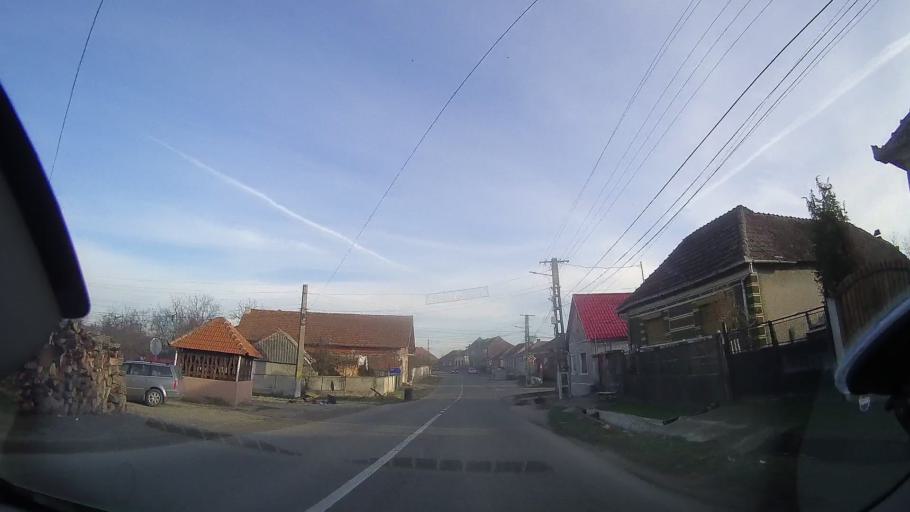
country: RO
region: Bihor
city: Lugasu de Jos
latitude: 47.0455
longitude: 22.3179
